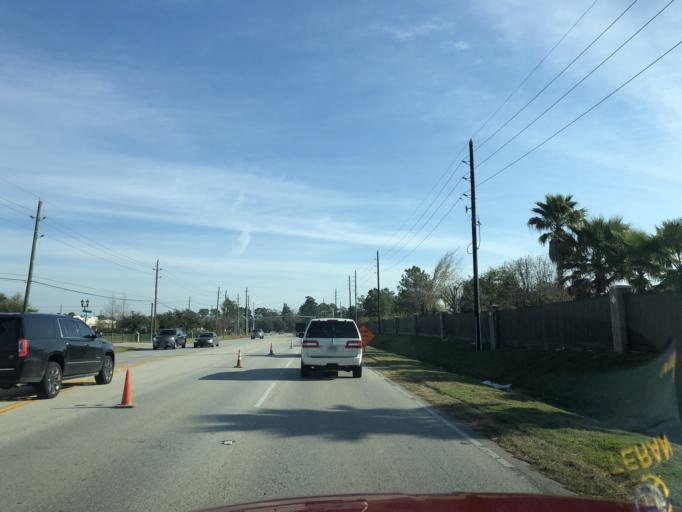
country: US
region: Texas
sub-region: Harris County
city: Tomball
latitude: 30.0372
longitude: -95.5501
